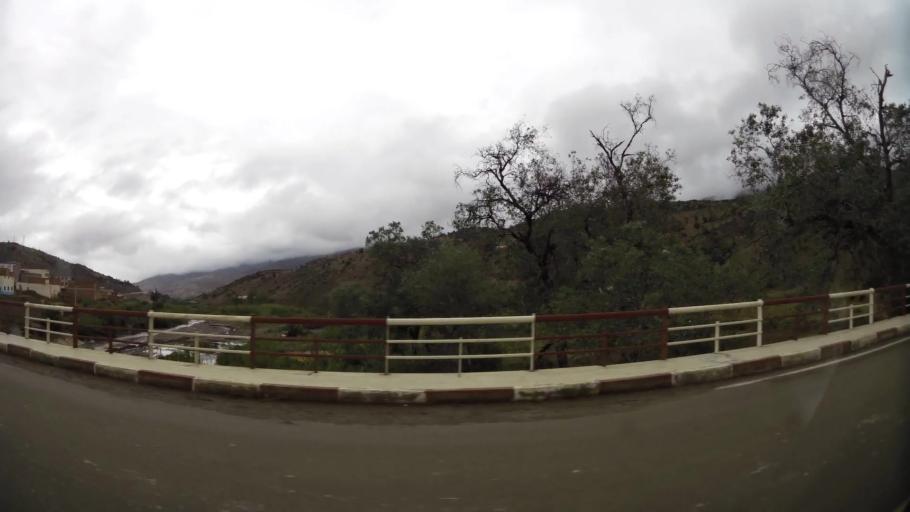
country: MA
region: Taza-Al Hoceima-Taounate
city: Imzourene
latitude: 34.9644
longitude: -3.8129
